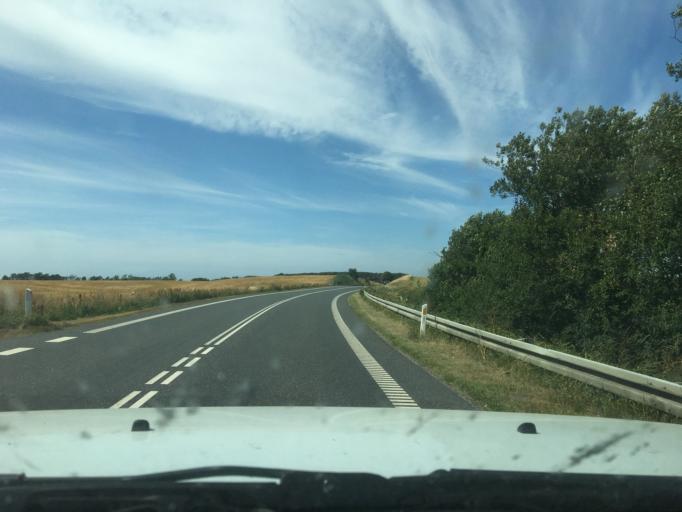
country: DK
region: Central Jutland
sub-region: Viborg Kommune
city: Viborg
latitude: 56.5803
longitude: 9.3740
